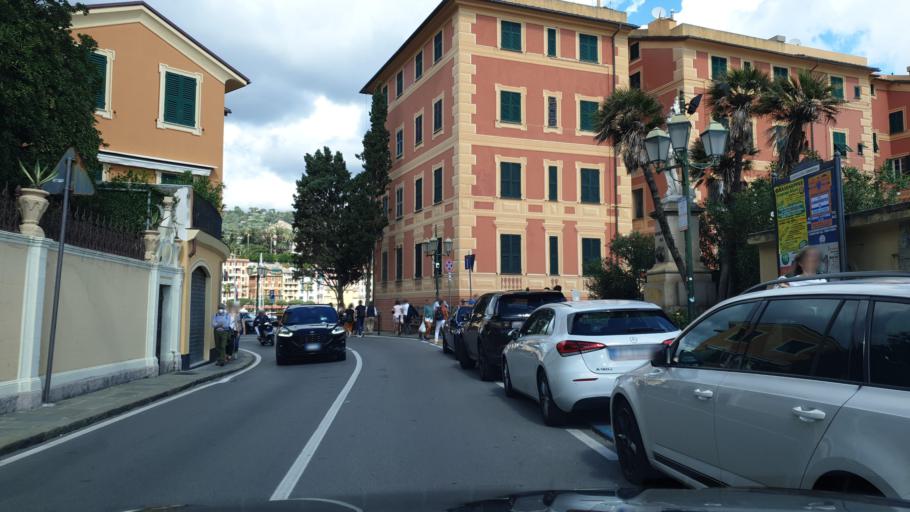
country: IT
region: Liguria
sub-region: Provincia di Genova
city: Santa Margherita Ligure
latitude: 44.3286
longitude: 9.2149
